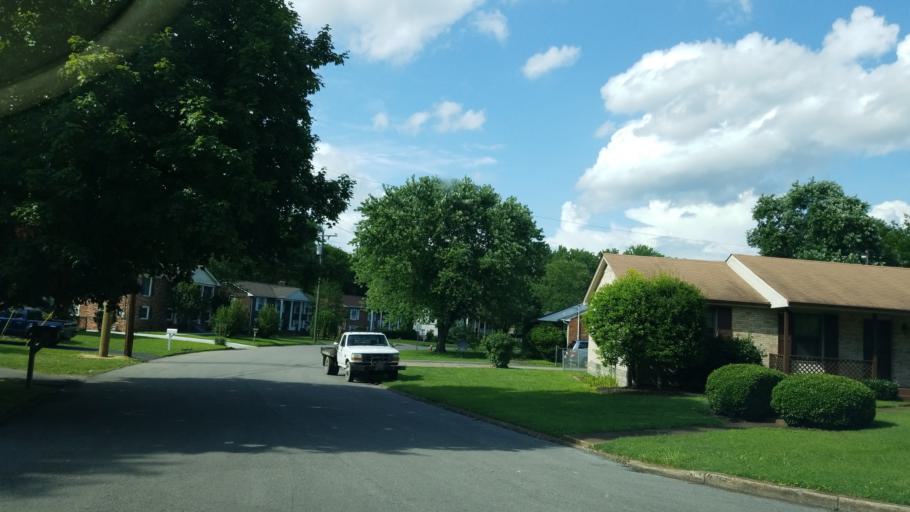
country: US
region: Tennessee
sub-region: Williamson County
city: Brentwood Estates
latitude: 36.0523
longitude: -86.6827
